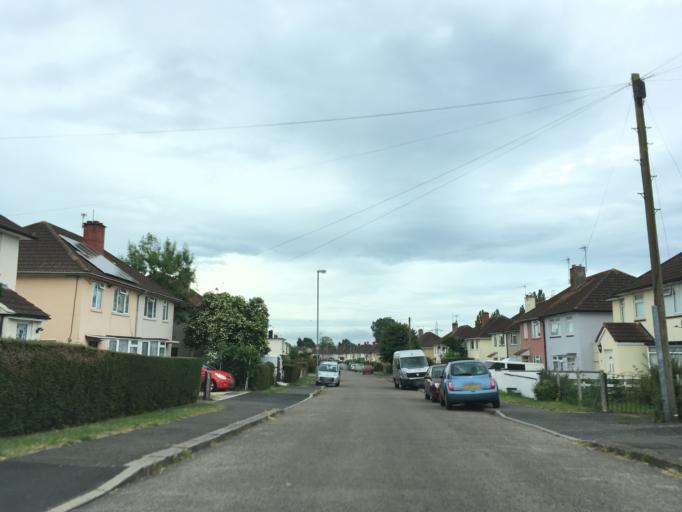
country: GB
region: England
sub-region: South Gloucestershire
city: Stoke Gifford
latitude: 51.4932
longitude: -2.5668
